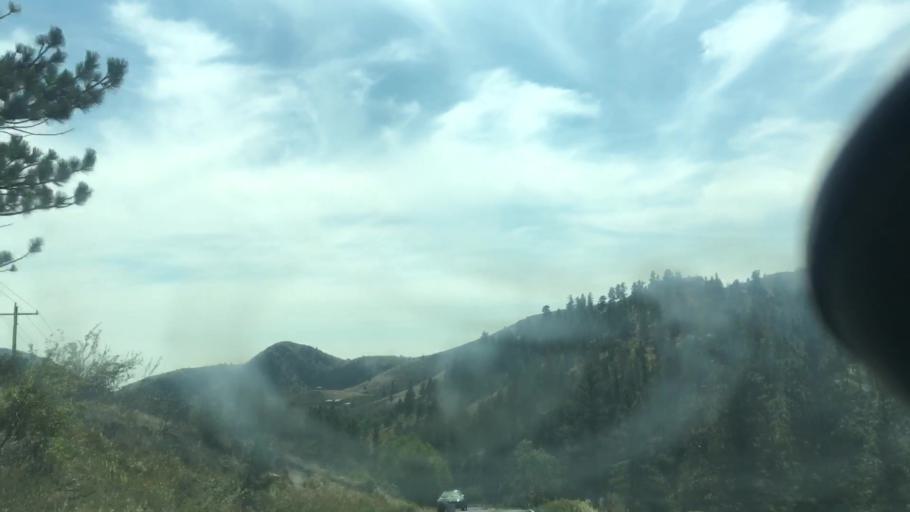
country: US
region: Colorado
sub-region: Larimer County
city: Laporte
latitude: 40.5766
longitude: -105.3287
